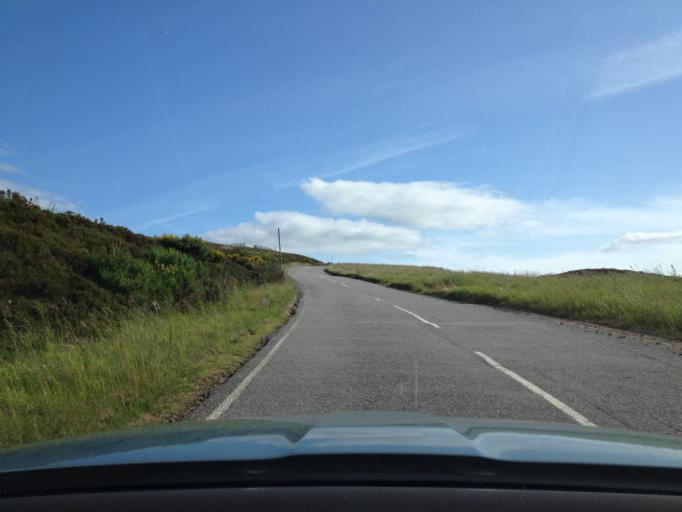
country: GB
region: Scotland
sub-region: Aberdeenshire
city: Laurencekirk
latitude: 56.9246
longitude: -2.5796
